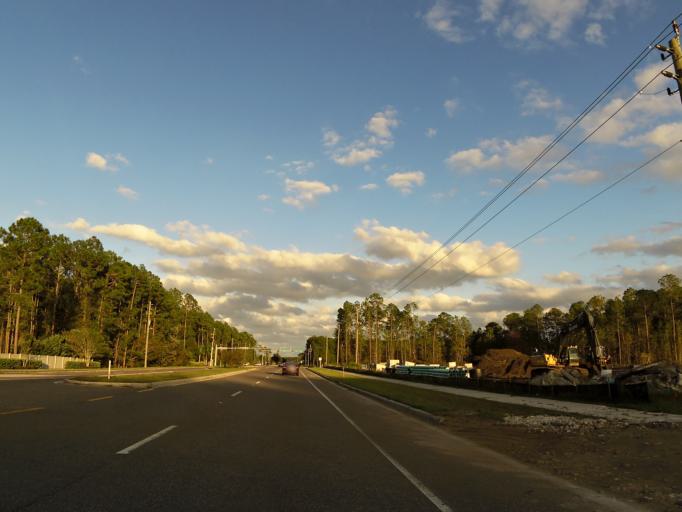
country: US
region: Florida
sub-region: Saint Johns County
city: Fruit Cove
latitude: 30.0598
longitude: -81.5270
